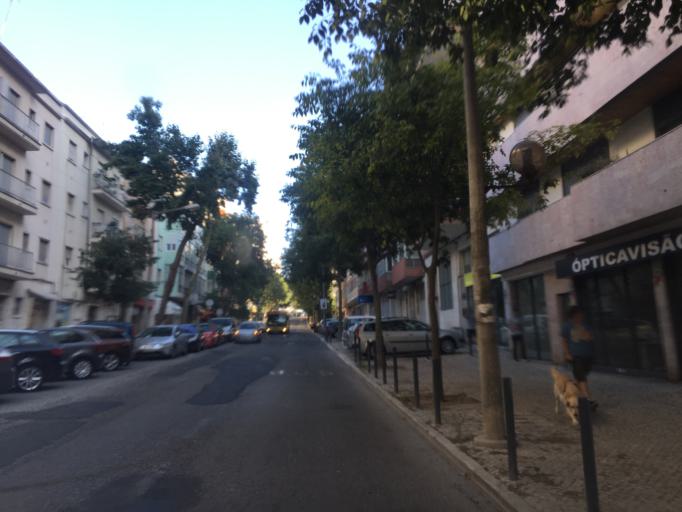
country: PT
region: Lisbon
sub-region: Odivelas
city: Pontinha
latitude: 38.7469
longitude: -9.1979
